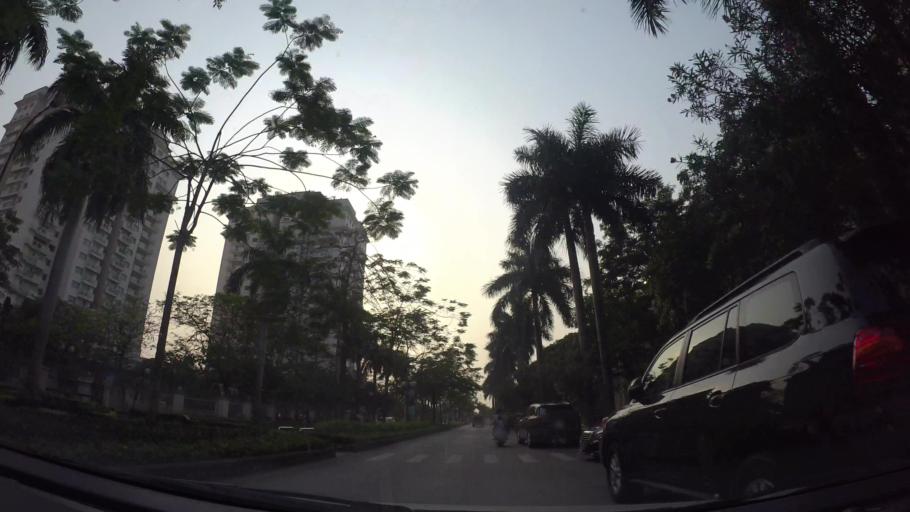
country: VN
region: Ha Noi
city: Tay Ho
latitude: 21.0744
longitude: 105.8024
